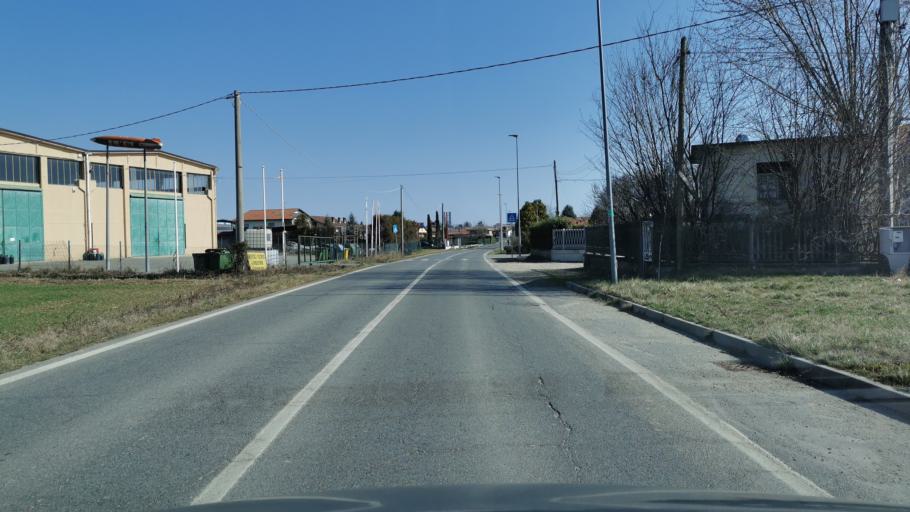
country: IT
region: Piedmont
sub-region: Provincia di Torino
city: Favria
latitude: 45.3298
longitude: 7.6769
